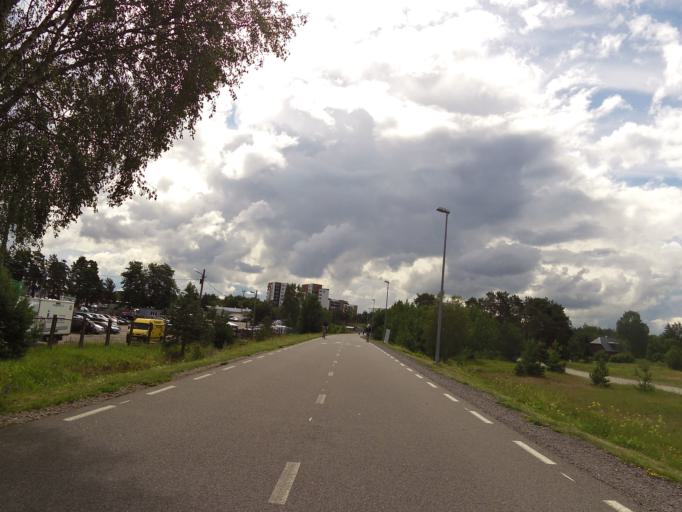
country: EE
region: Harju
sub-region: Saue vald
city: Laagri
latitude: 59.4014
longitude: 24.6439
